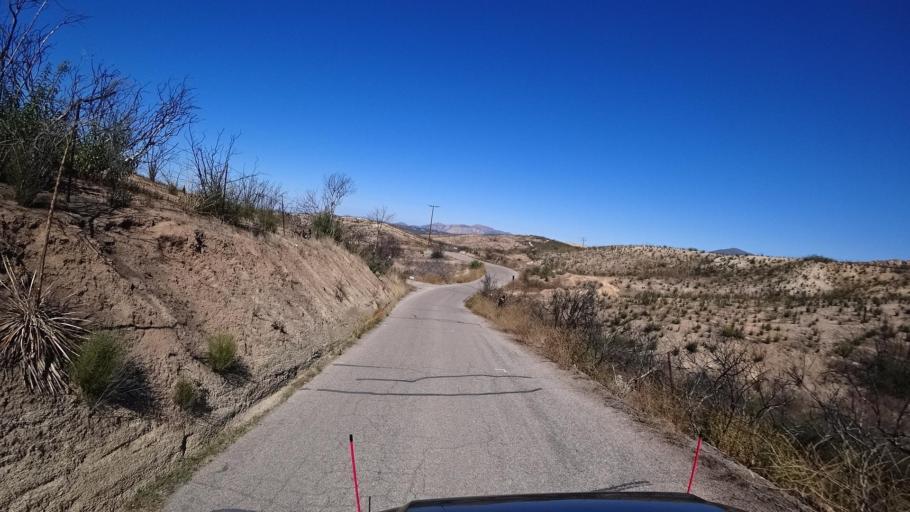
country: US
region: California
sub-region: San Diego County
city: Alpine
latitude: 32.7714
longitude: -116.7630
